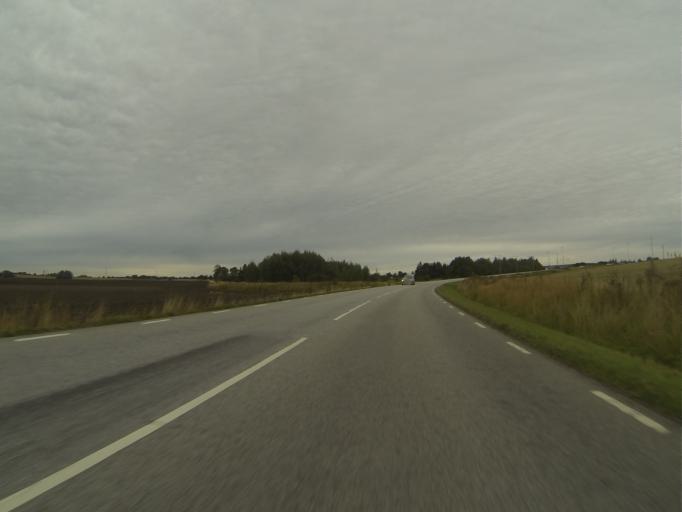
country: SE
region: Skane
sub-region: Staffanstorps Kommun
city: Staffanstorp
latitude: 55.6245
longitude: 13.1880
